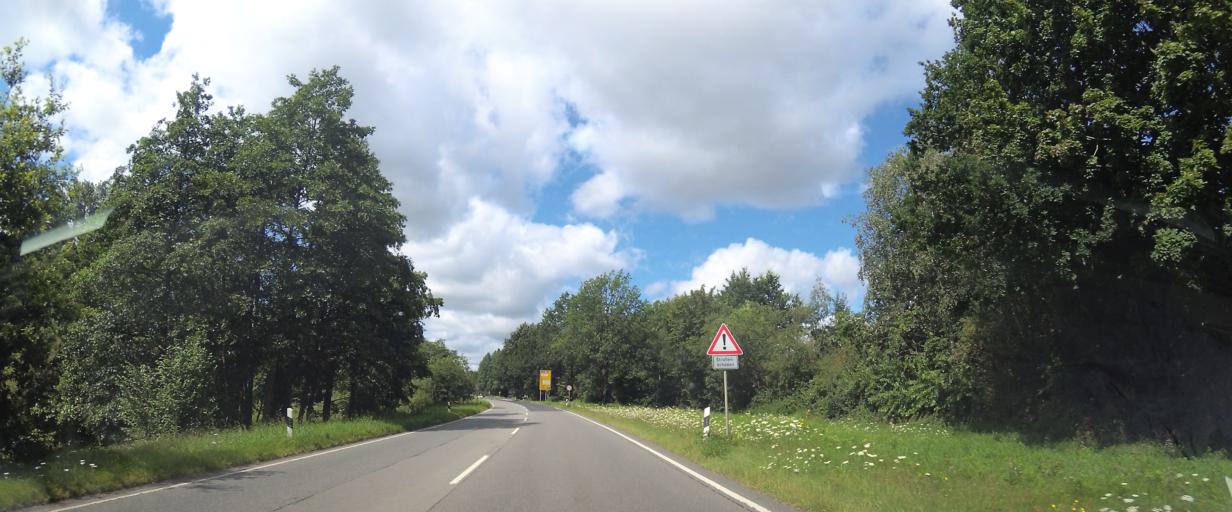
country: DE
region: Lower Saxony
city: Haren
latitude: 52.7891
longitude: 7.2694
